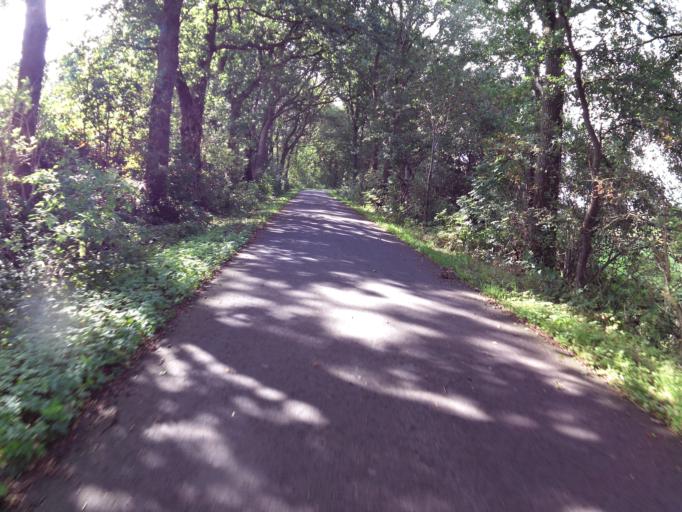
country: DE
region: Lower Saxony
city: Sandbostel
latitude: 53.4390
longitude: 9.1251
